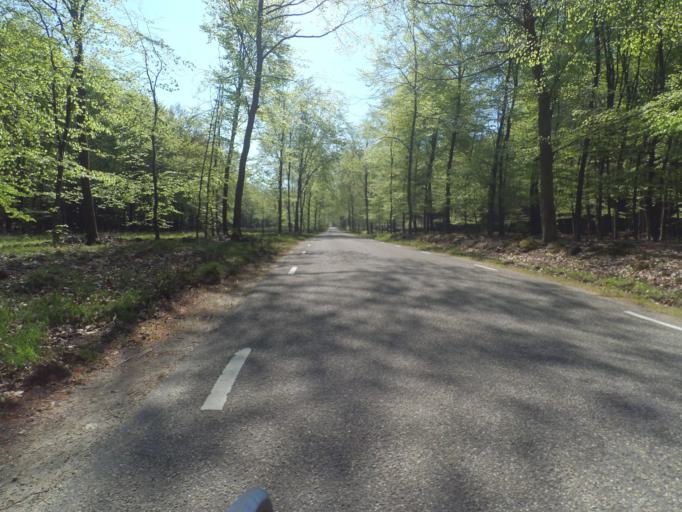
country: NL
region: Gelderland
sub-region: Gemeente Apeldoorn
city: Uddel
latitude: 52.2300
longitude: 5.8674
